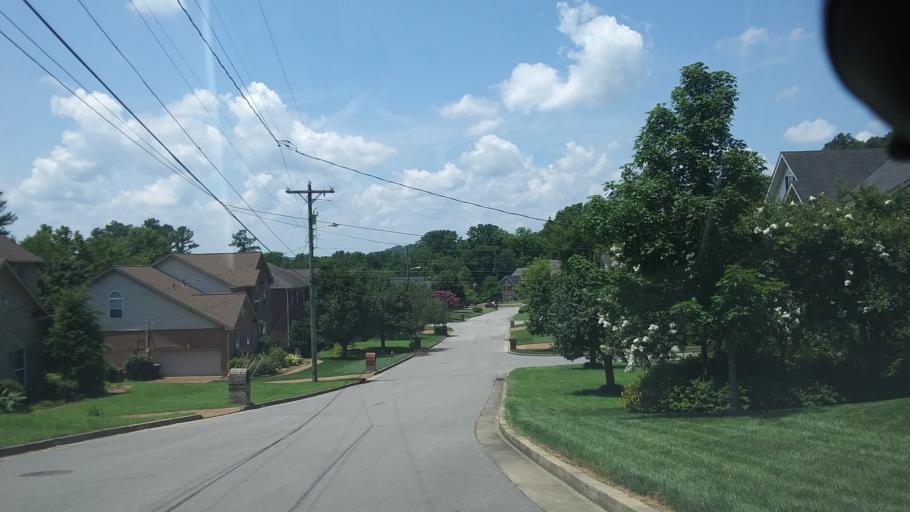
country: US
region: Tennessee
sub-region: Davidson County
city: Belle Meade
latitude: 36.0910
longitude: -86.9429
